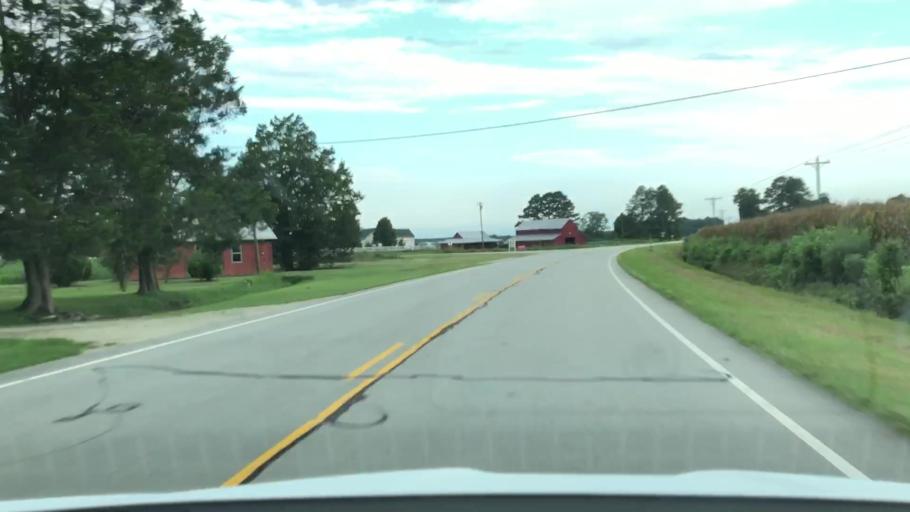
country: US
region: North Carolina
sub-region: Jones County
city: Trenton
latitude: 35.0963
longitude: -77.4810
